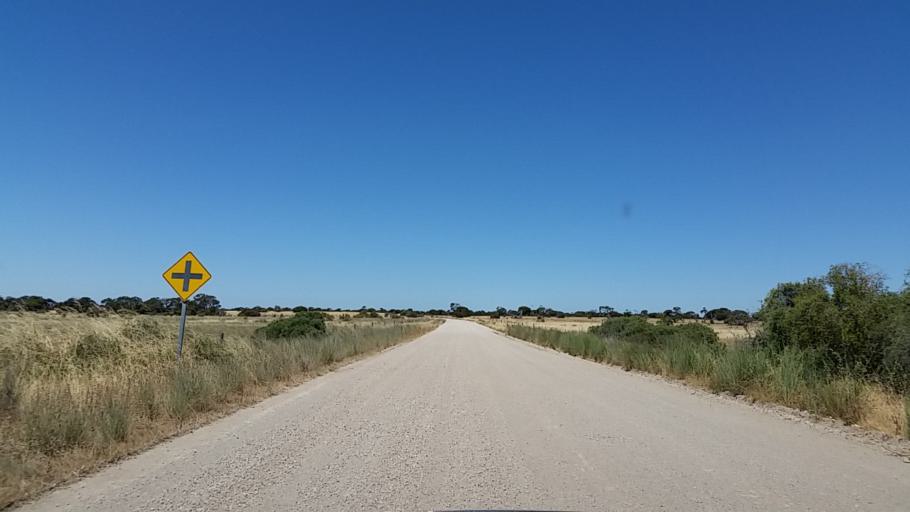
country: AU
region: South Australia
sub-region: Yorke Peninsula
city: Honiton
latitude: -35.0803
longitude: 137.4834
